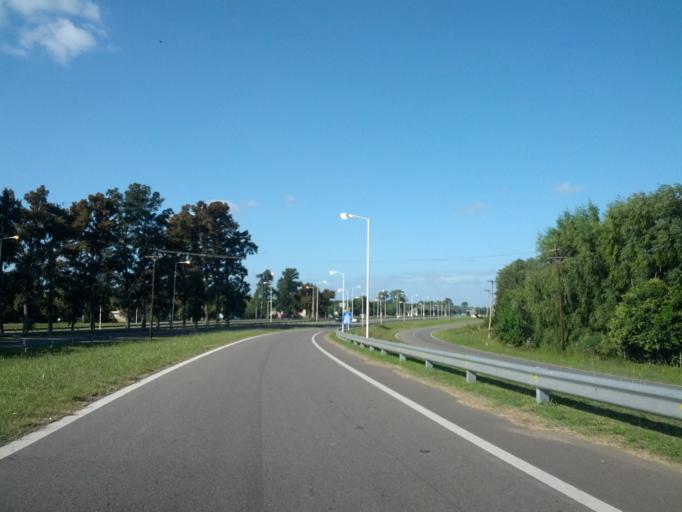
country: AR
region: Buenos Aires
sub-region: Partido de Mercedes
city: Mercedes
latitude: -34.6568
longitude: -59.3536
